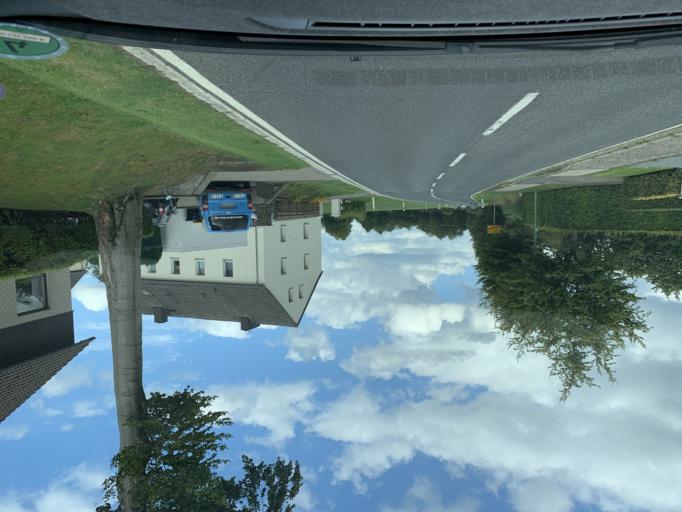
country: DE
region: North Rhine-Westphalia
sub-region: Regierungsbezirk Koln
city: Simmerath
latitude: 50.5948
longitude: 6.2620
